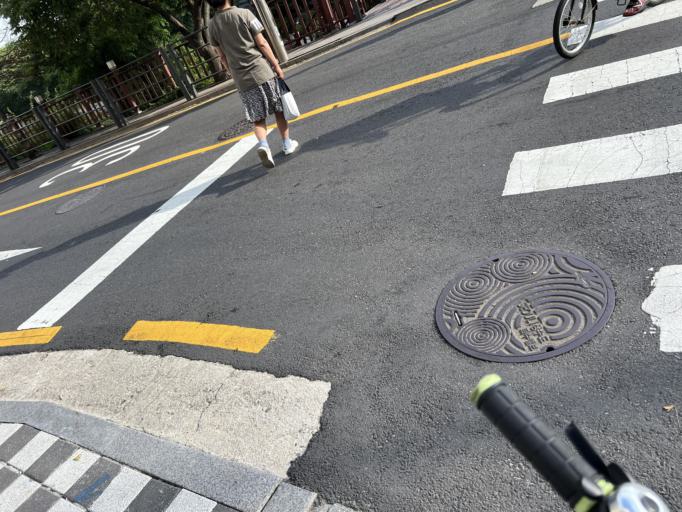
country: KR
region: Seoul
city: Seoul
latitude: 37.6371
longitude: 127.0368
